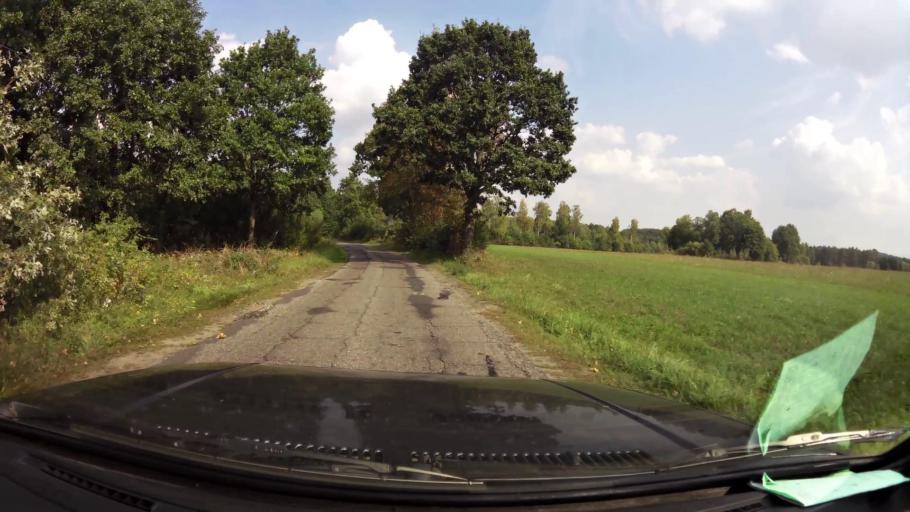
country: PL
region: West Pomeranian Voivodeship
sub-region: Powiat koszalinski
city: Polanow
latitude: 54.1261
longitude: 16.5183
